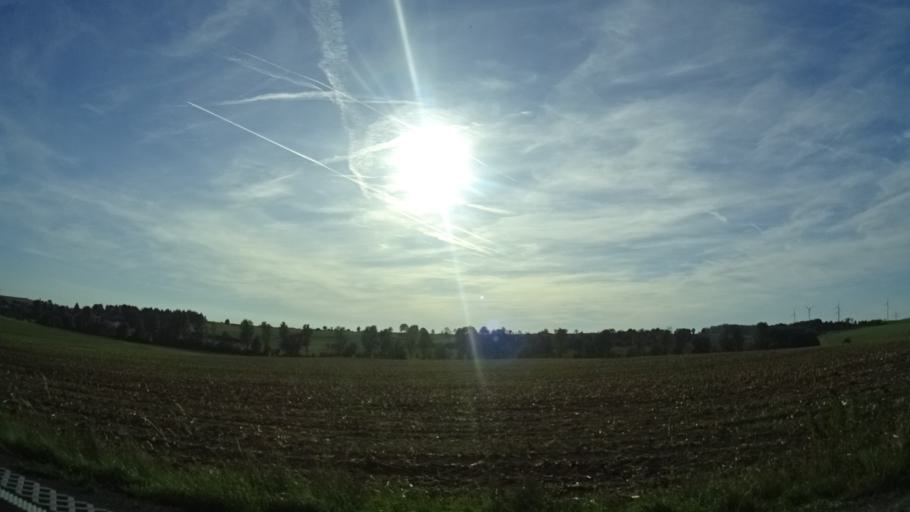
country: DE
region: Hesse
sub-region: Regierungsbezirk Giessen
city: Freiensteinau
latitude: 50.3813
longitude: 9.4287
